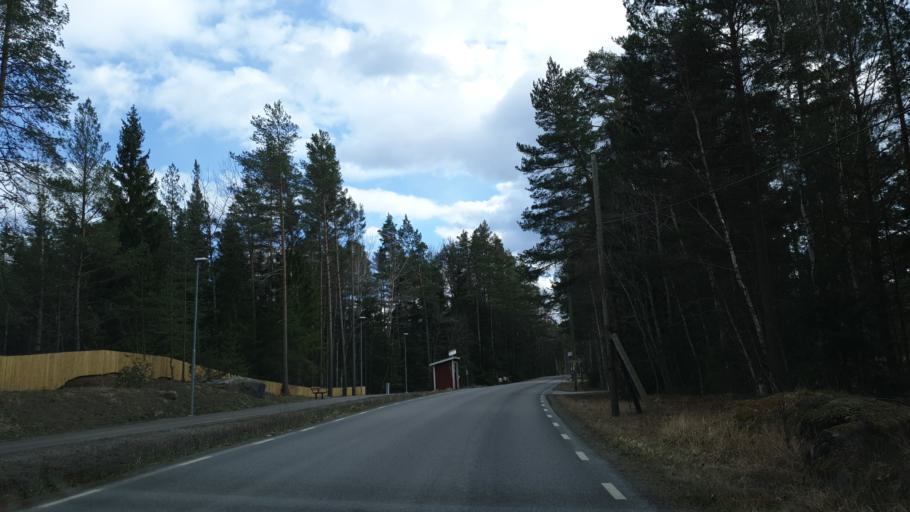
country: SE
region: Stockholm
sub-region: Varmdo Kommun
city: Mortnas
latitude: 59.2687
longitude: 18.4277
